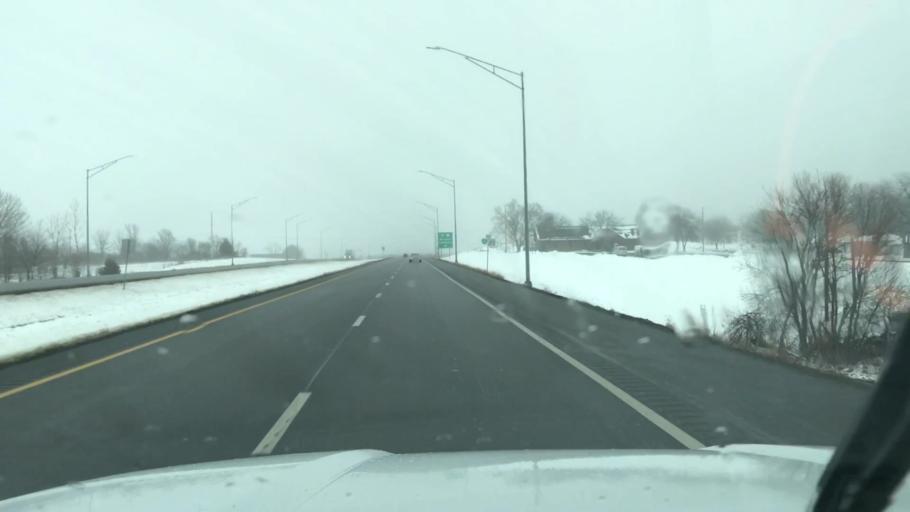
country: US
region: Missouri
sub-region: Clinton County
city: Cameron
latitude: 39.7543
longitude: -94.2425
